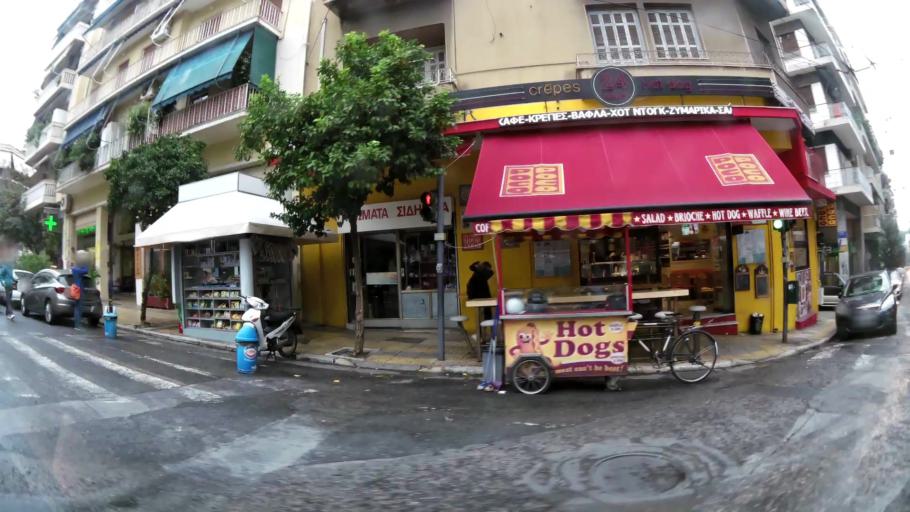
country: GR
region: Attica
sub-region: Nomarchia Athinas
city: Vyronas
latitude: 37.9683
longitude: 23.7439
